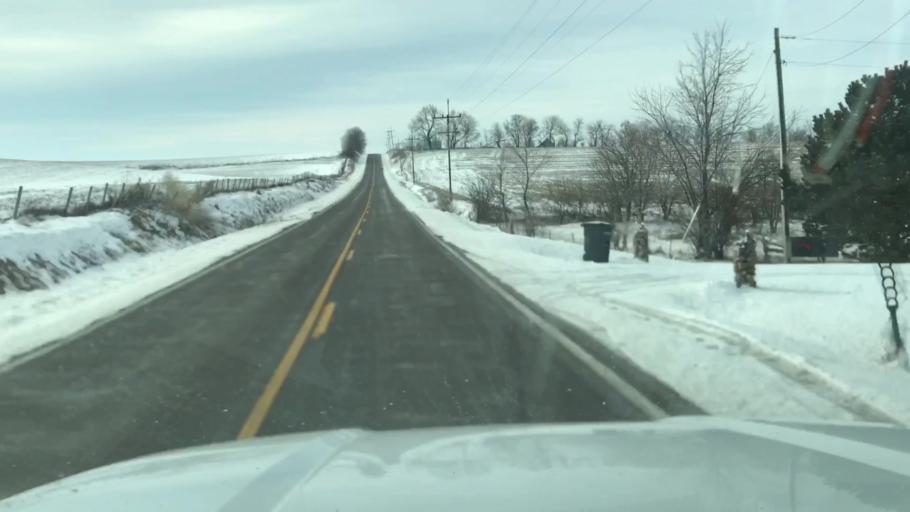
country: US
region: Missouri
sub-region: Holt County
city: Oregon
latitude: 40.0753
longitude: -95.1355
